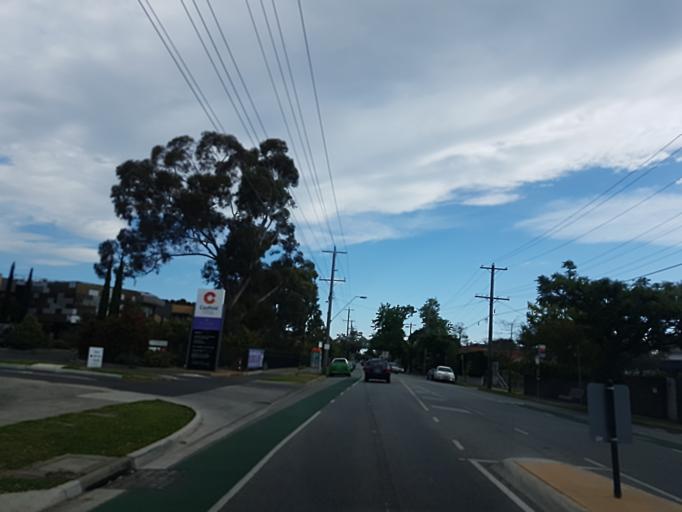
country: AU
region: Victoria
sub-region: Glen Eira
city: Caulfield
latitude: -37.8834
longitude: 145.0155
